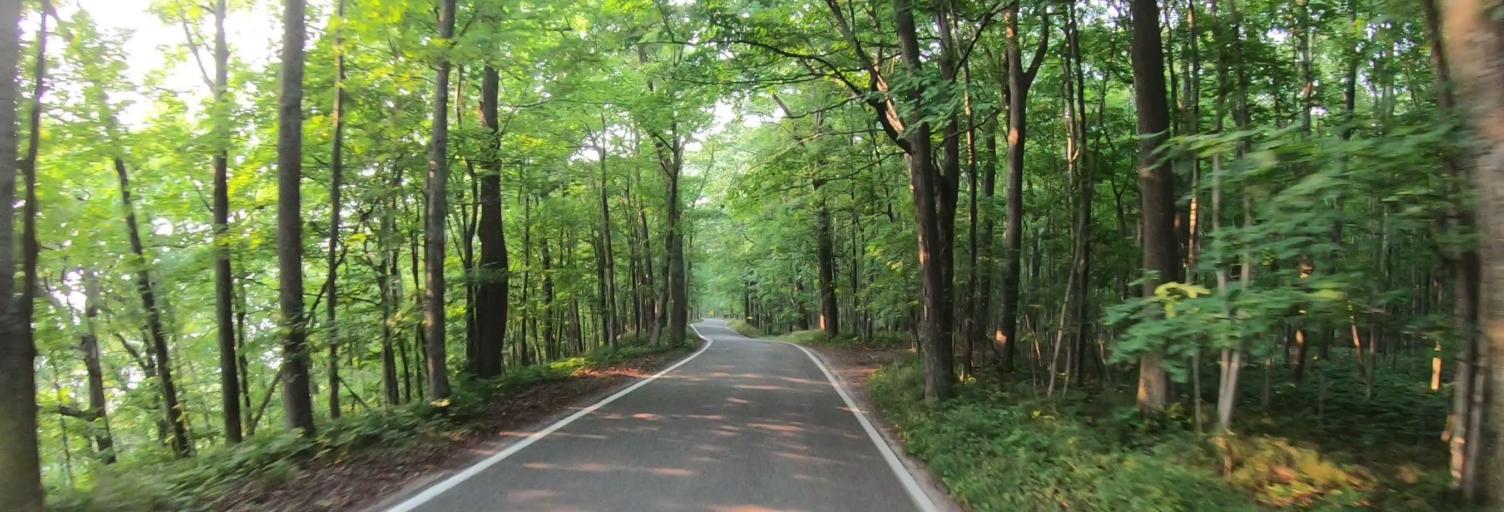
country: US
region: Michigan
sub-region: Emmet County
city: Harbor Springs
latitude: 45.5337
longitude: -85.1112
